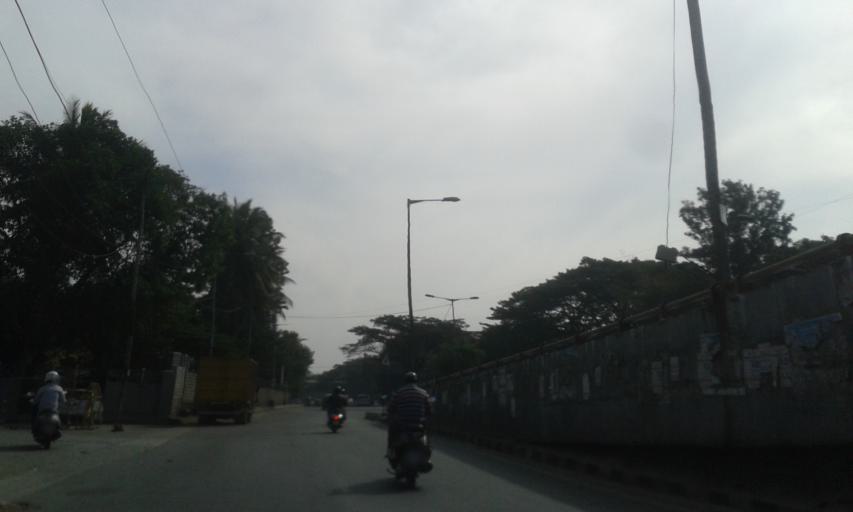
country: IN
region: Karnataka
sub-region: Bangalore Urban
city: Bangalore
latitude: 12.9371
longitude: 77.6030
